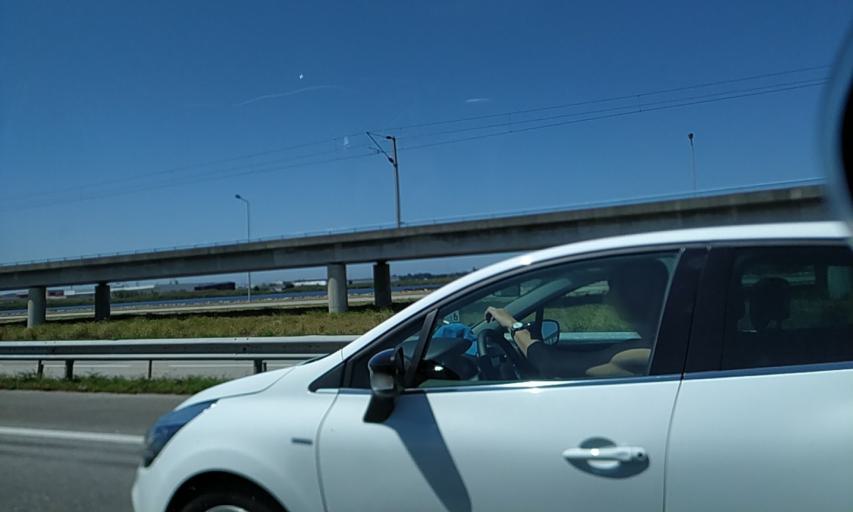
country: PT
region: Aveiro
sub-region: Aveiro
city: Aveiro
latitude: 40.6388
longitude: -8.6652
